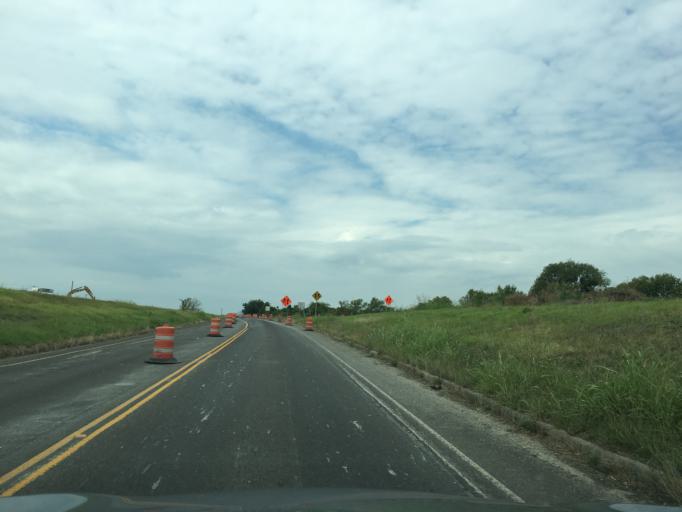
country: US
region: Texas
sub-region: Collin County
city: Melissa
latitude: 33.2713
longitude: -96.5817
